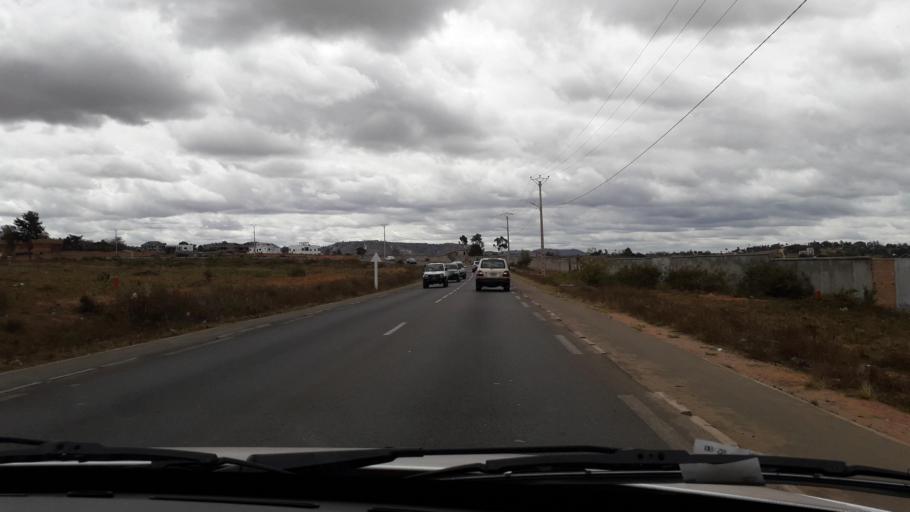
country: MG
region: Analamanga
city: Antananarivo
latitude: -18.8066
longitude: 47.4939
